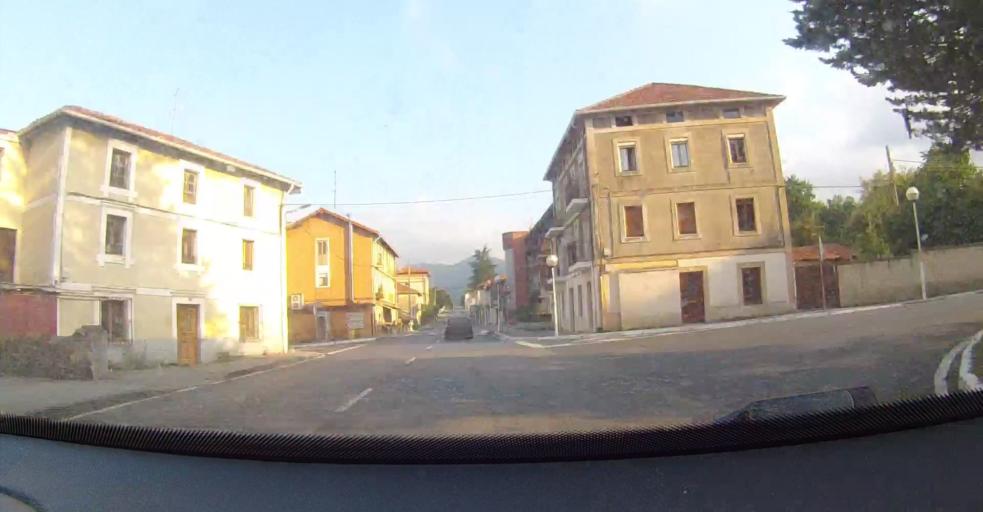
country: ES
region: Basque Country
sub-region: Bizkaia
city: Sopuerta
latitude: 43.2744
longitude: -3.1569
